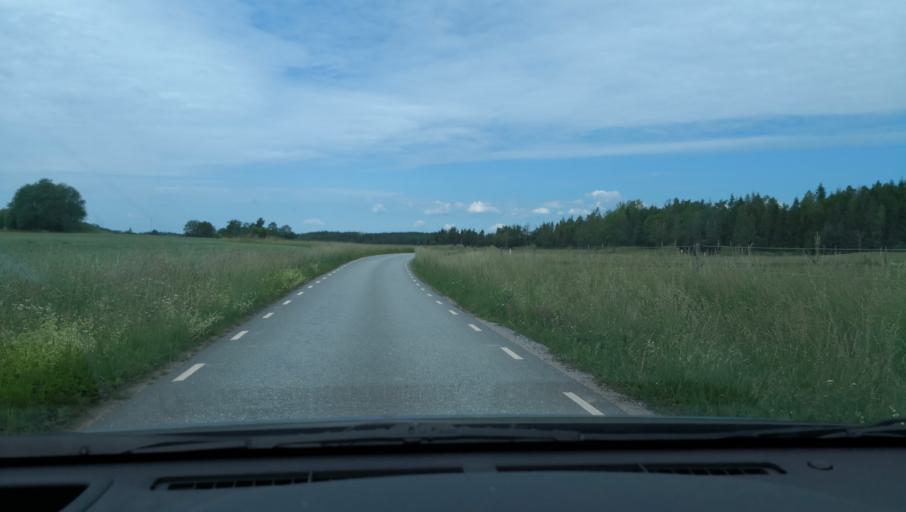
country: SE
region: Uppsala
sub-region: Habo Kommun
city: Balsta
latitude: 59.6974
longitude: 17.4801
